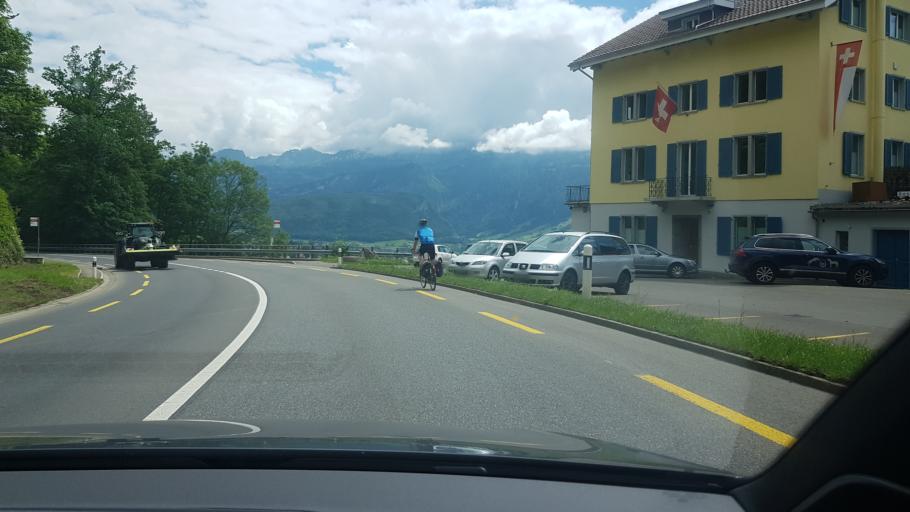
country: CH
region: Schwyz
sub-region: Bezirk Schwyz
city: Steinen
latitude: 47.0474
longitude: 8.6290
